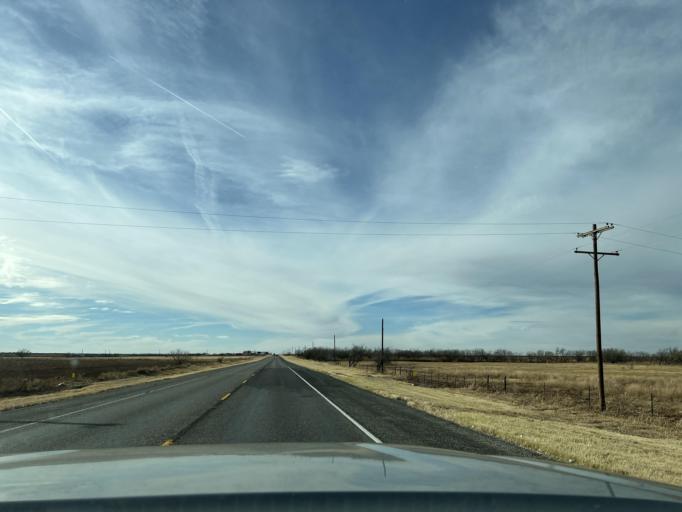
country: US
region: Texas
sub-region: Jones County
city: Anson
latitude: 32.7520
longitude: -99.9319
